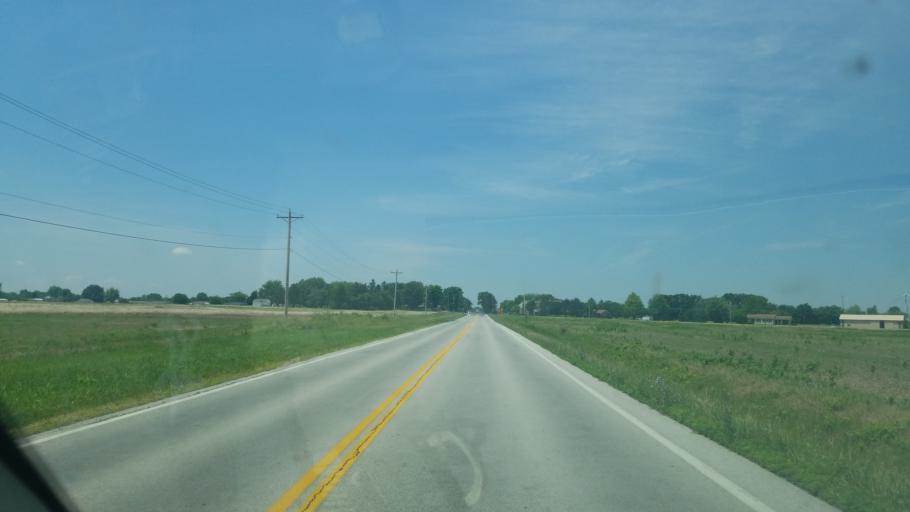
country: US
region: Ohio
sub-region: Hancock County
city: Findlay
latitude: 41.0729
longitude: -83.6215
